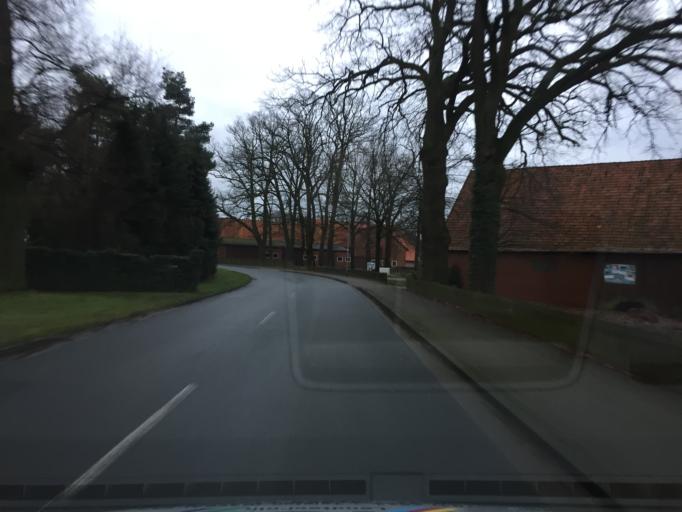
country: DE
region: Lower Saxony
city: Borstel
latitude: 52.6669
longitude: 8.9723
